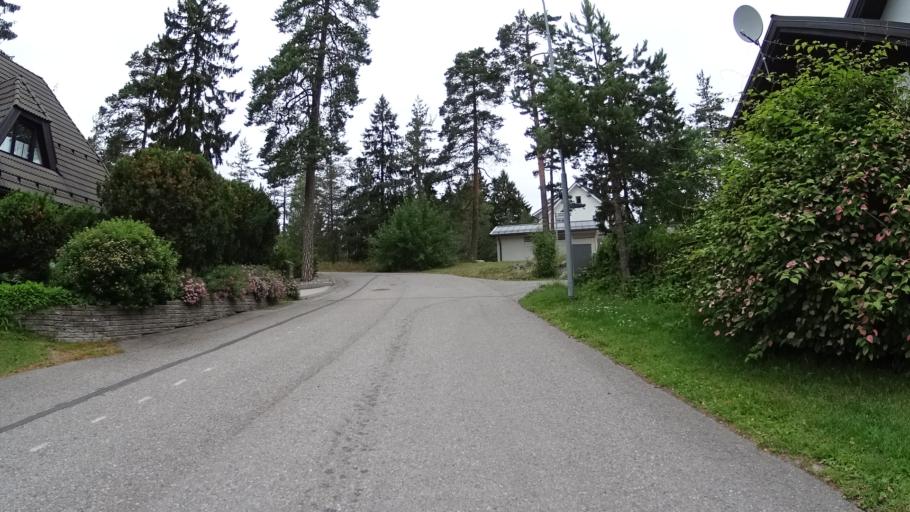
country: FI
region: Uusimaa
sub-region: Helsinki
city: Kauniainen
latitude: 60.2193
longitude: 24.7056
